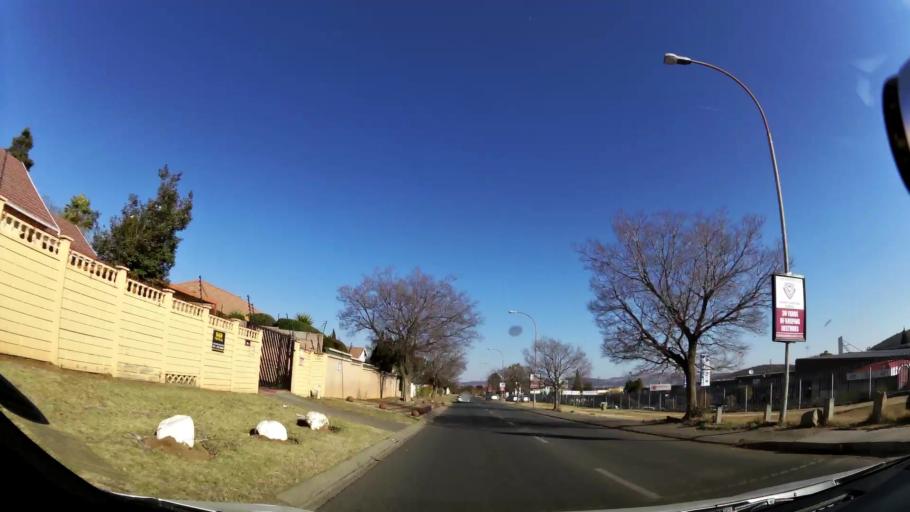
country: ZA
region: Gauteng
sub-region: City of Johannesburg Metropolitan Municipality
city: Johannesburg
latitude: -26.3002
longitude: 28.0539
